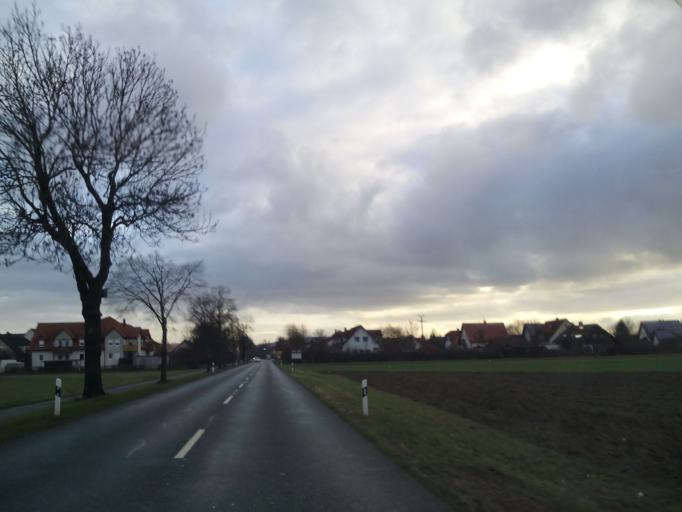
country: DE
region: Bavaria
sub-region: Upper Franconia
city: Michelau
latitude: 50.1639
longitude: 11.0960
